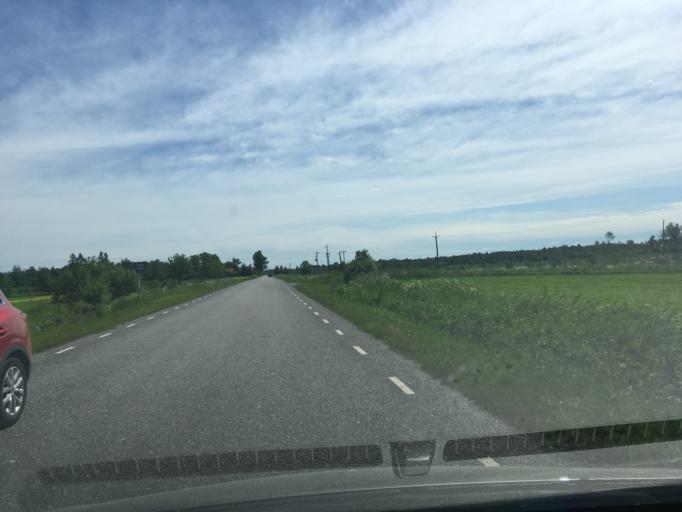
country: EE
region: Paernumaa
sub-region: Audru vald
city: Audru
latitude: 58.4306
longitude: 24.4005
